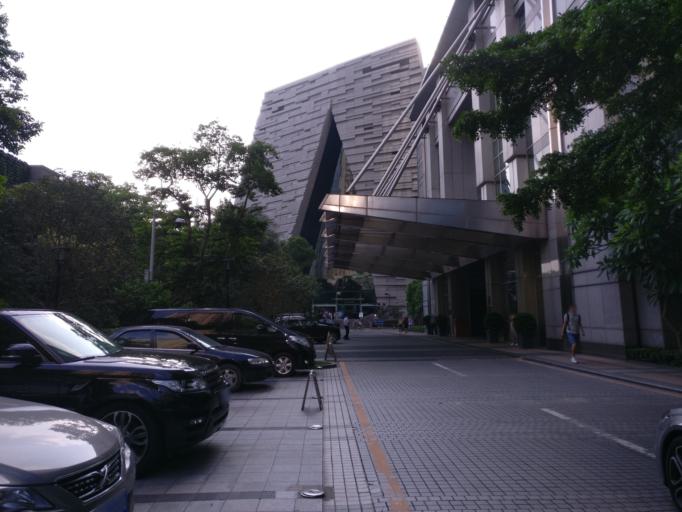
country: CN
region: Guangdong
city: Wushan
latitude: 23.1186
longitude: 113.3223
